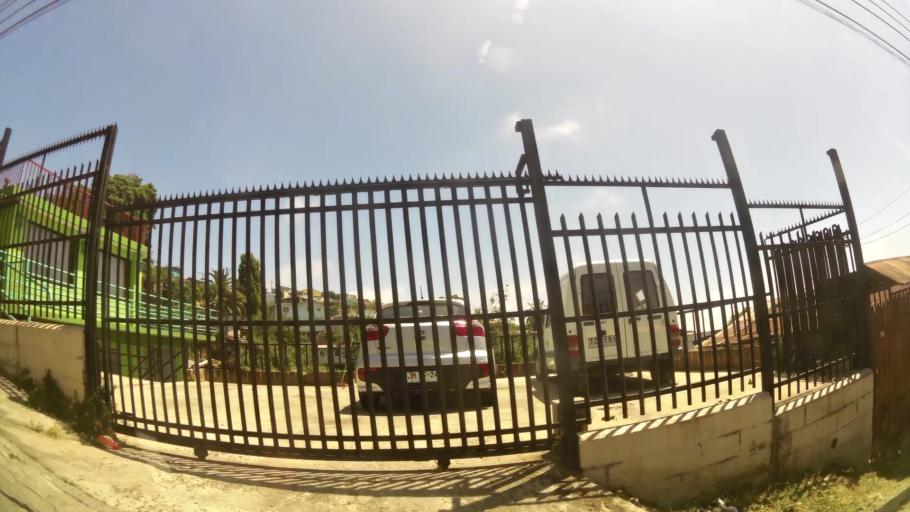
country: CL
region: Valparaiso
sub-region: Provincia de Valparaiso
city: Valparaiso
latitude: -33.0386
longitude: -71.6383
